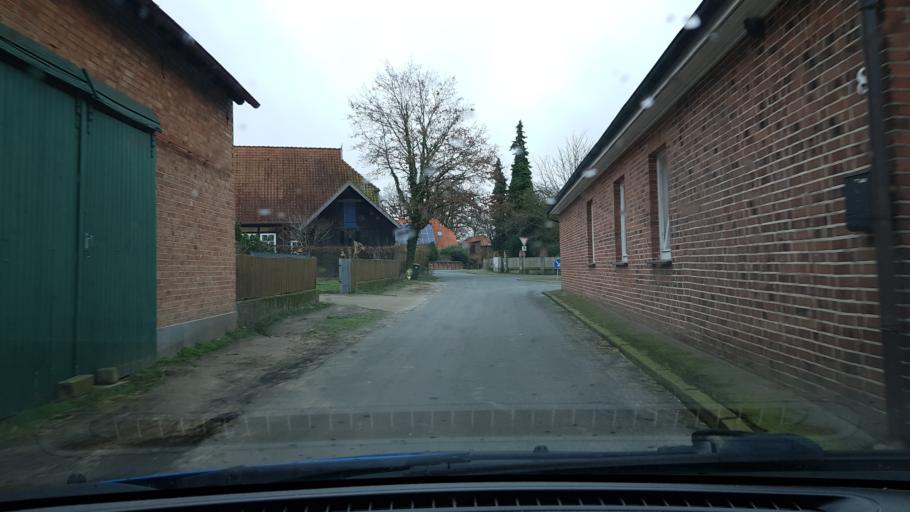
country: DE
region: Lower Saxony
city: Emmendorf
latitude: 53.0043
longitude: 10.6049
